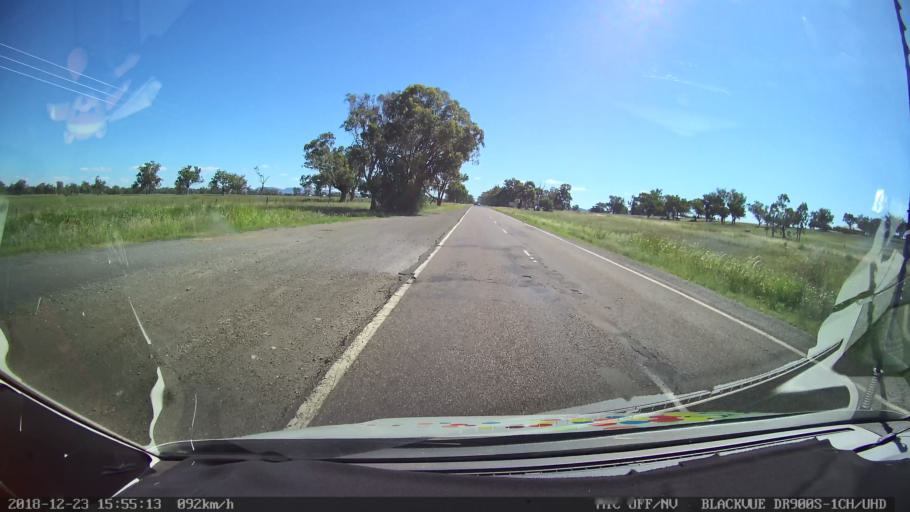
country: AU
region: New South Wales
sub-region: Tamworth Municipality
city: Phillip
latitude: -31.1532
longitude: 150.8706
